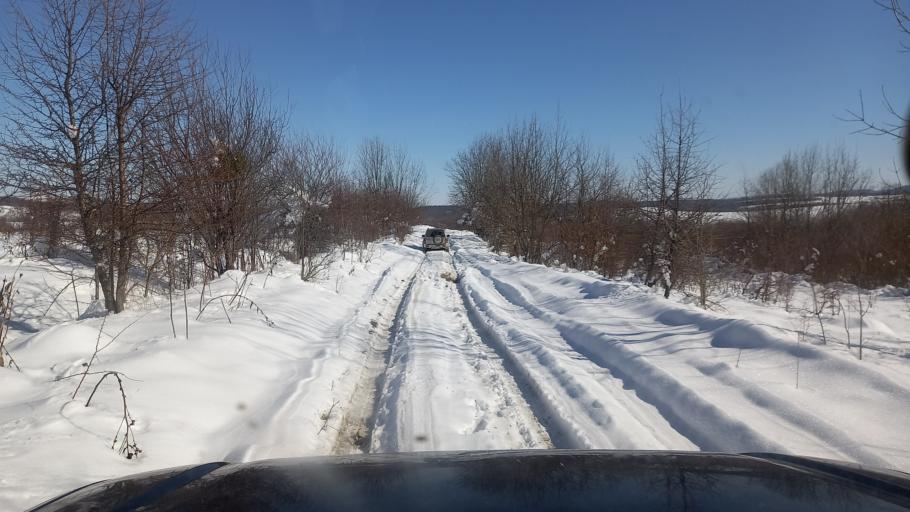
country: RU
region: Krasnodarskiy
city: Gubskaya
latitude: 44.3394
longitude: 40.4396
